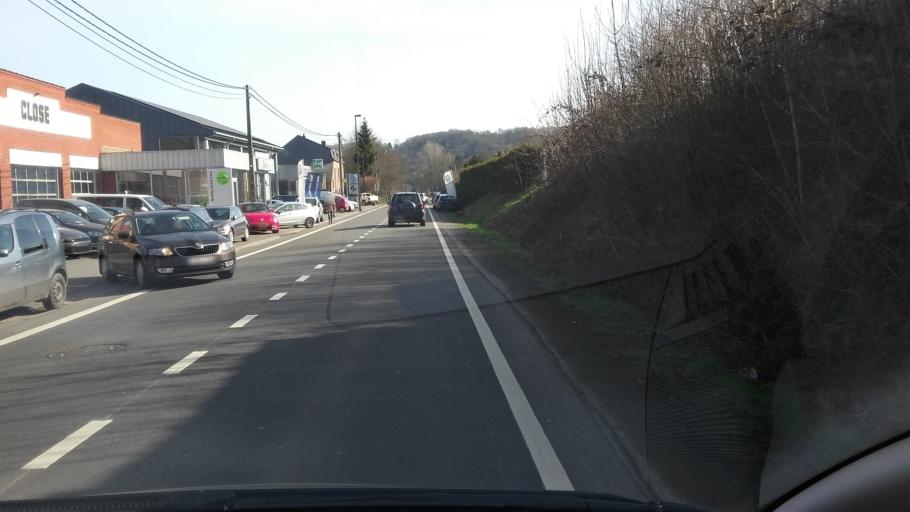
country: BE
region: Wallonia
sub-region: Province de Liege
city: Hamoir
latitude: 50.3797
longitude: 5.5245
